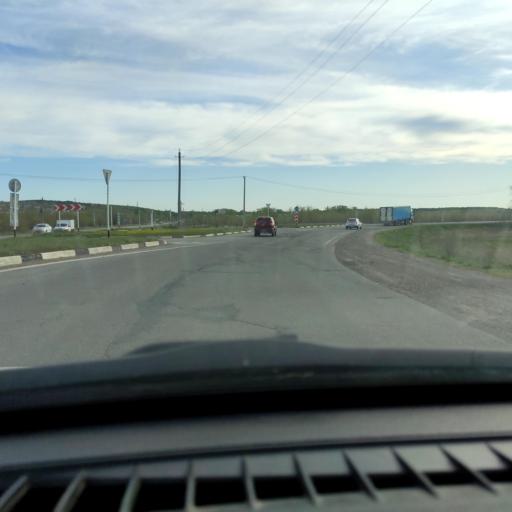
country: RU
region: Samara
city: Mirnyy
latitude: 53.4978
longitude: 50.2612
